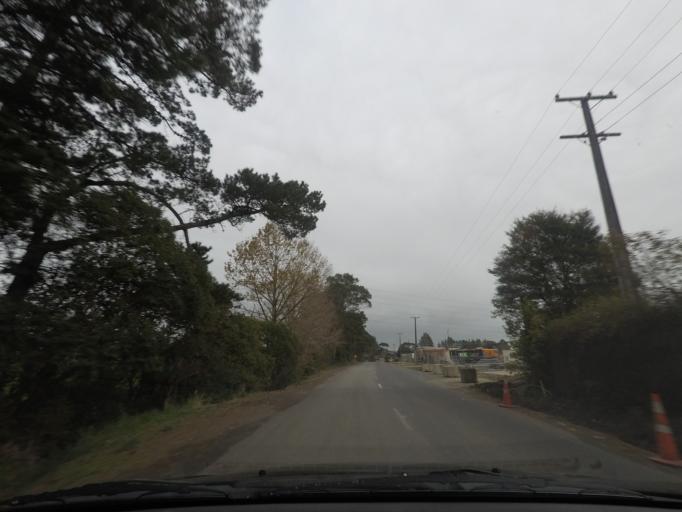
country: NZ
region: Auckland
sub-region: Auckland
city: Muriwai Beach
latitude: -36.7600
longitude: 174.5755
